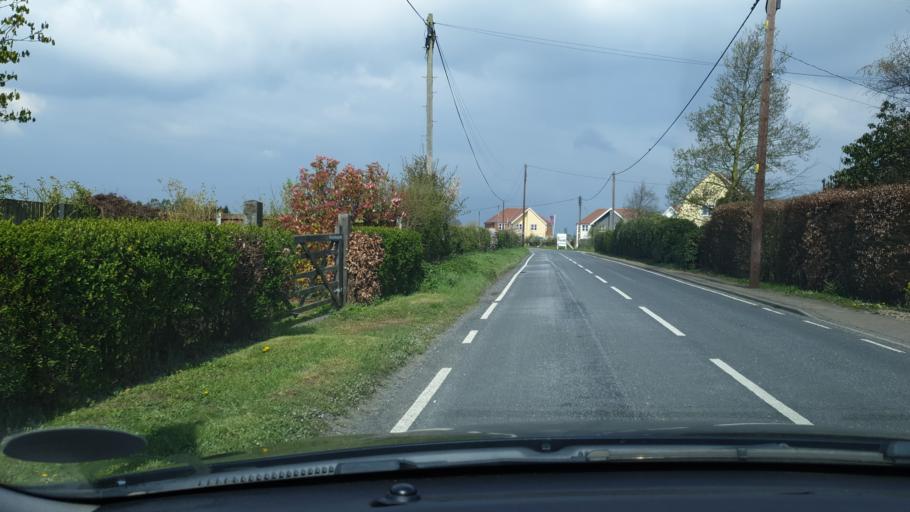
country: GB
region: England
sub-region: Essex
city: Great Bentley
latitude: 51.8906
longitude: 1.1084
